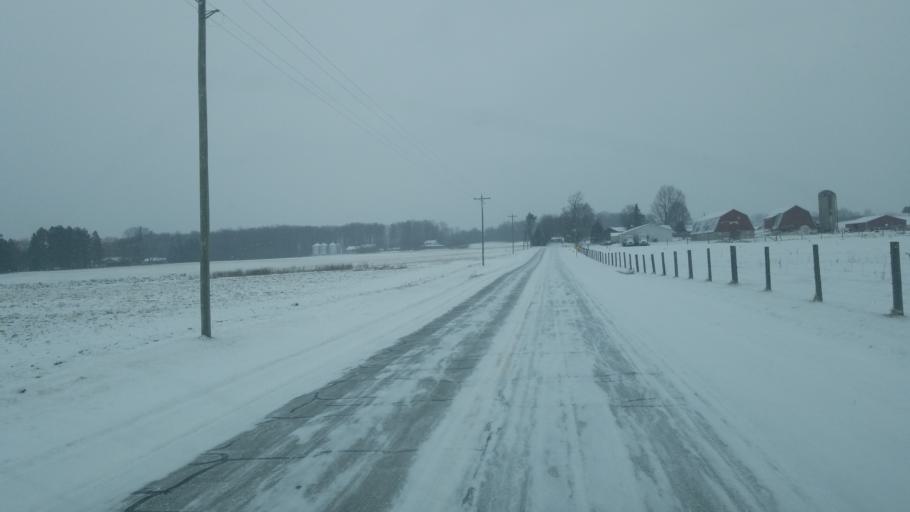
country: US
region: Michigan
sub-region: Osceola County
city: Reed City
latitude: 43.8189
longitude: -85.4040
